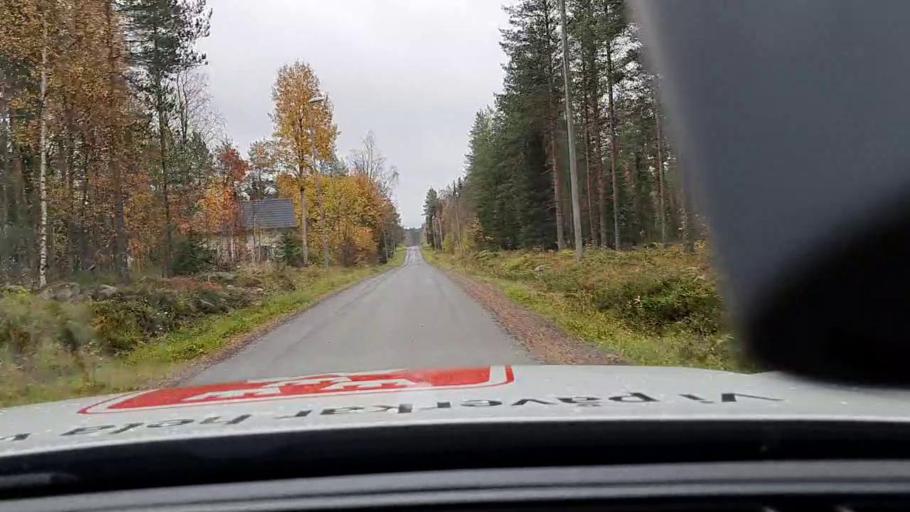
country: FI
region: Lapland
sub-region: Kemi-Tornio
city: Tornio
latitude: 65.9783
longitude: 24.0144
